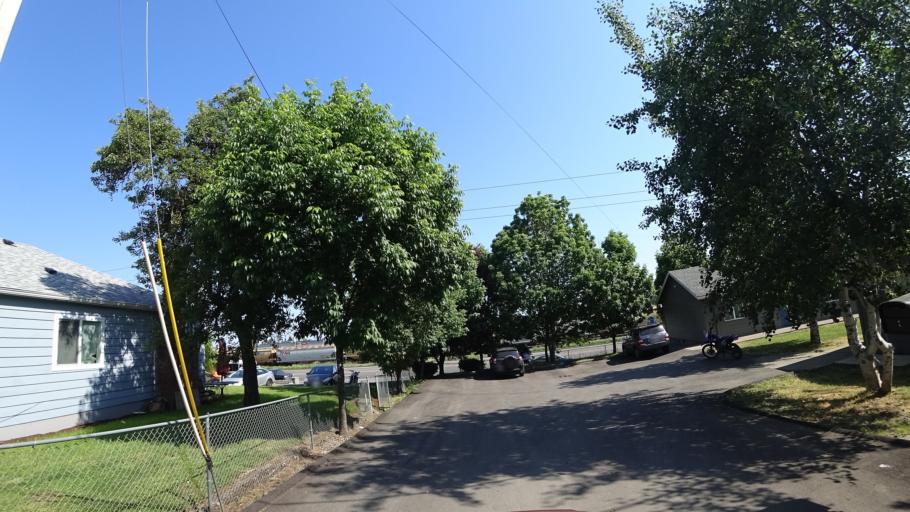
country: US
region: Oregon
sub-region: Multnomah County
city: Portland
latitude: 45.5752
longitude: -122.6466
